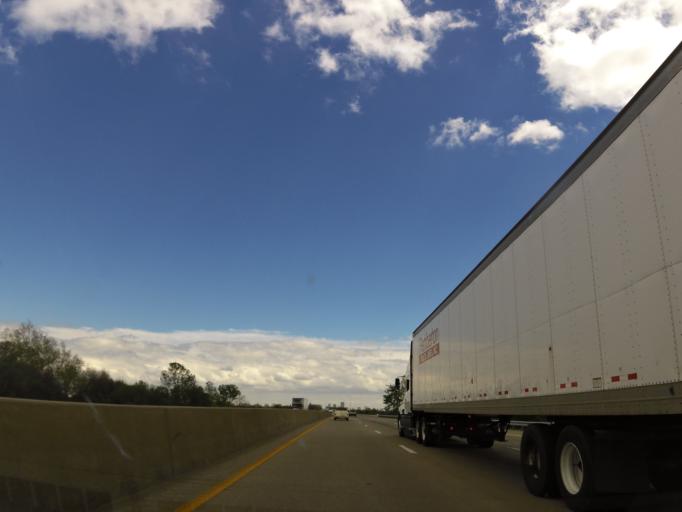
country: US
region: Tennessee
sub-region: Shelby County
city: Memphis
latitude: 35.1554
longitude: -90.1155
